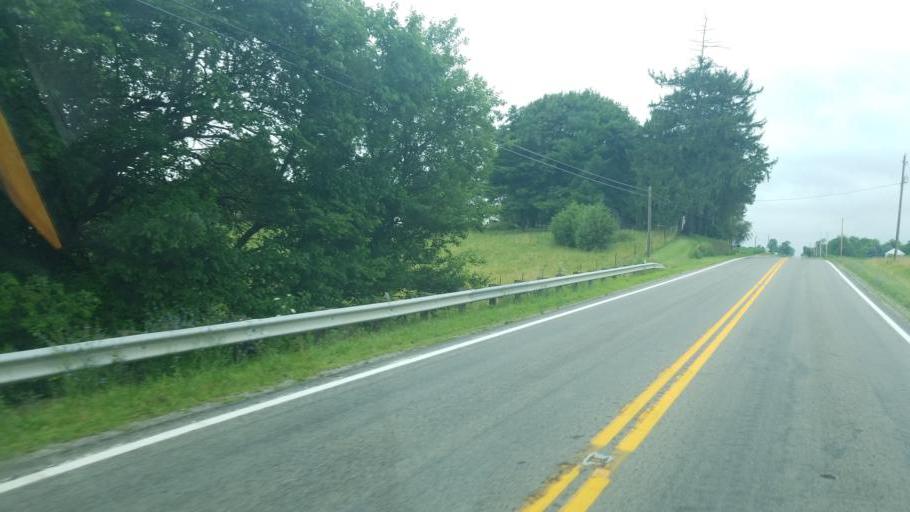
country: US
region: Ohio
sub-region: Hardin County
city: Kenton
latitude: 40.6100
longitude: -83.6880
